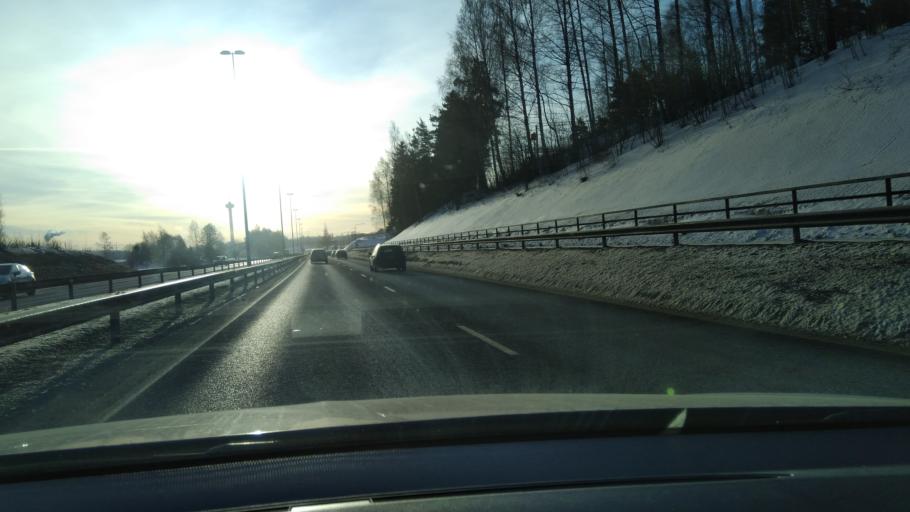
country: FI
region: Pirkanmaa
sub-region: Tampere
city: Tampere
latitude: 61.5077
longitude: 23.7034
